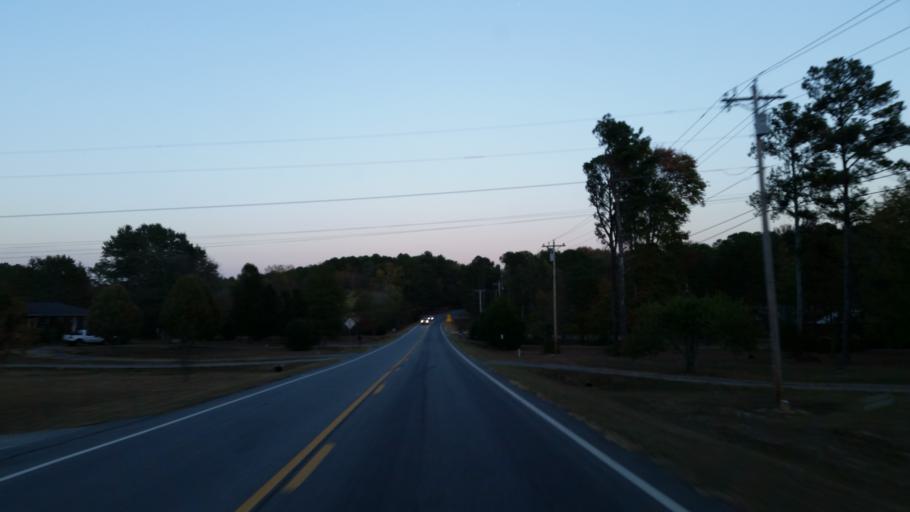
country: US
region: Georgia
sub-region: Gordon County
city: Calhoun
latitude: 34.5727
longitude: -84.9696
